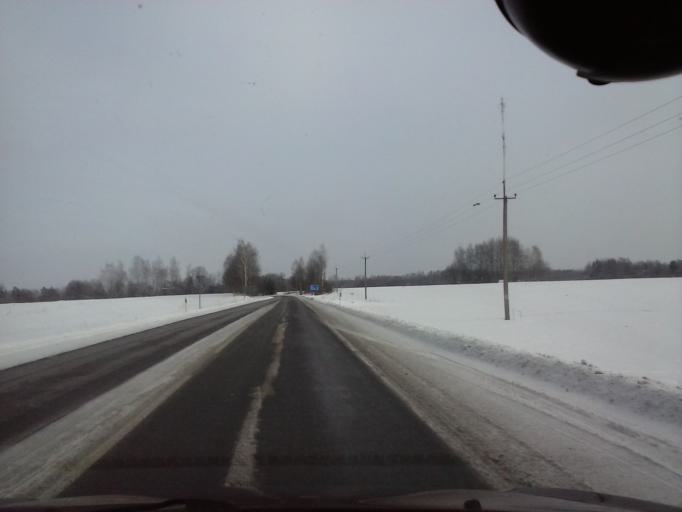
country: EE
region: Paernumaa
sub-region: Saarde vald
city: Kilingi-Nomme
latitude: 58.1573
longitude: 24.9953
